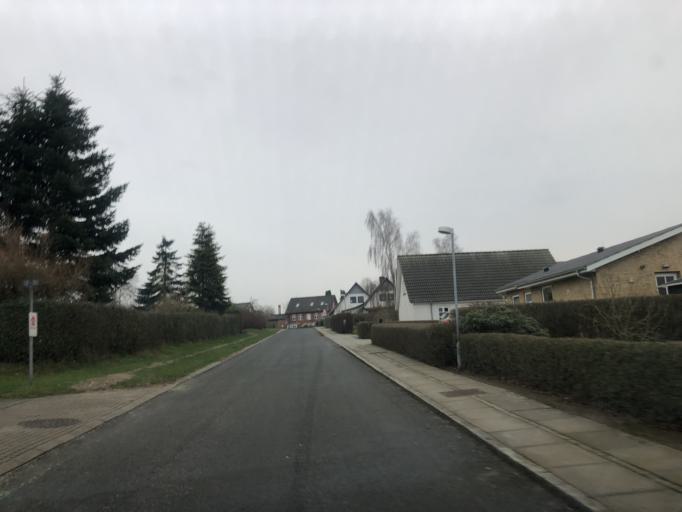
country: DK
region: South Denmark
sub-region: Faaborg-Midtfyn Kommune
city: Arslev
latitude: 55.2985
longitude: 10.4605
